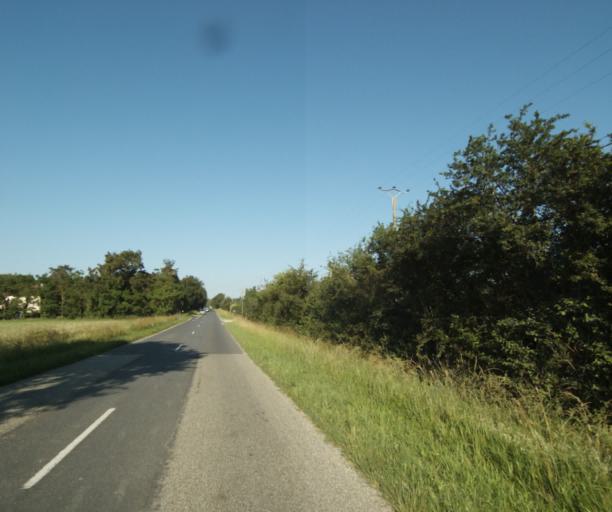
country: FR
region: Midi-Pyrenees
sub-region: Departement du Tarn-et-Garonne
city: Montauban
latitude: 44.0362
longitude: 1.4032
